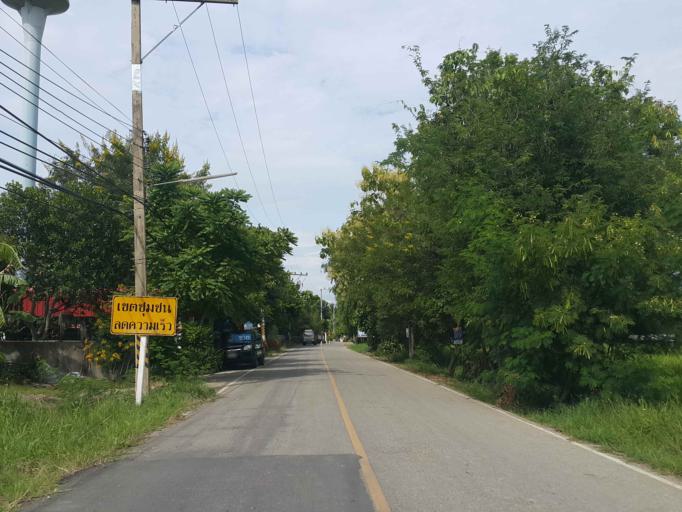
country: TH
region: Chiang Mai
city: Saraphi
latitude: 18.7307
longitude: 99.0581
